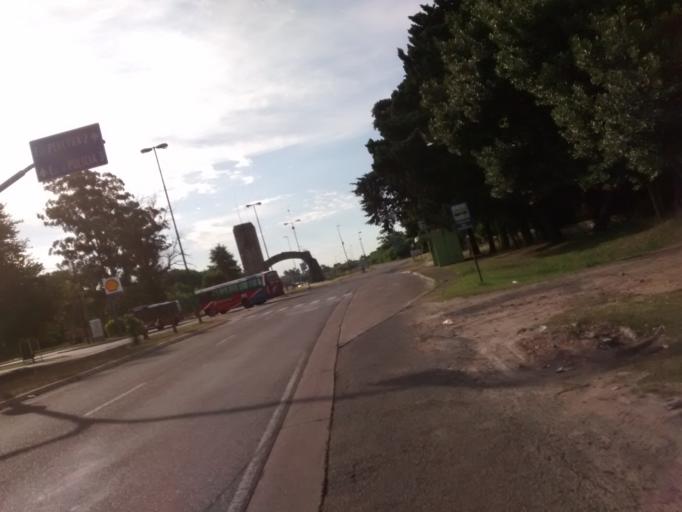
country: AR
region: Buenos Aires
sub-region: Partido de La Plata
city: La Plata
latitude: -34.8481
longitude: -58.0979
